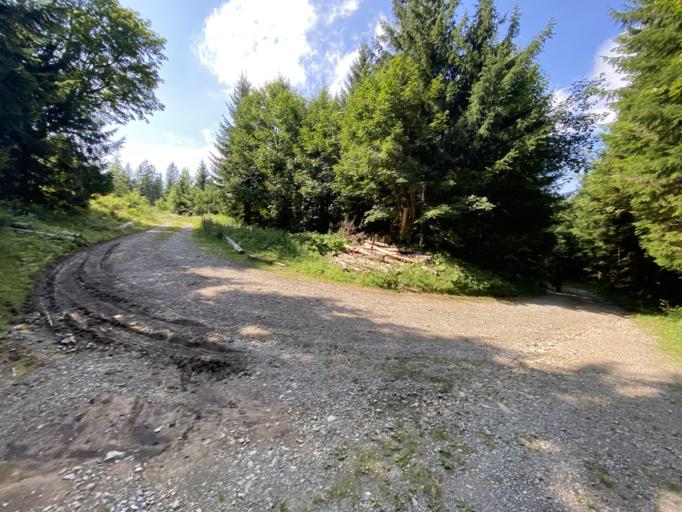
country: AT
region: Lower Austria
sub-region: Politischer Bezirk Lilienfeld
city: Annaberg
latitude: 47.8860
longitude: 15.3396
